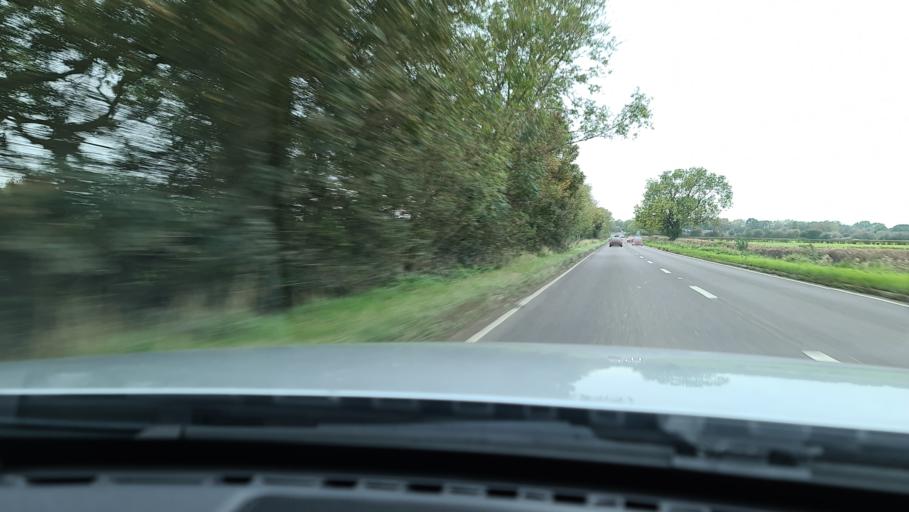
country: GB
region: England
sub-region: Oxfordshire
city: Bicester
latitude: 51.8777
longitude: -1.1022
